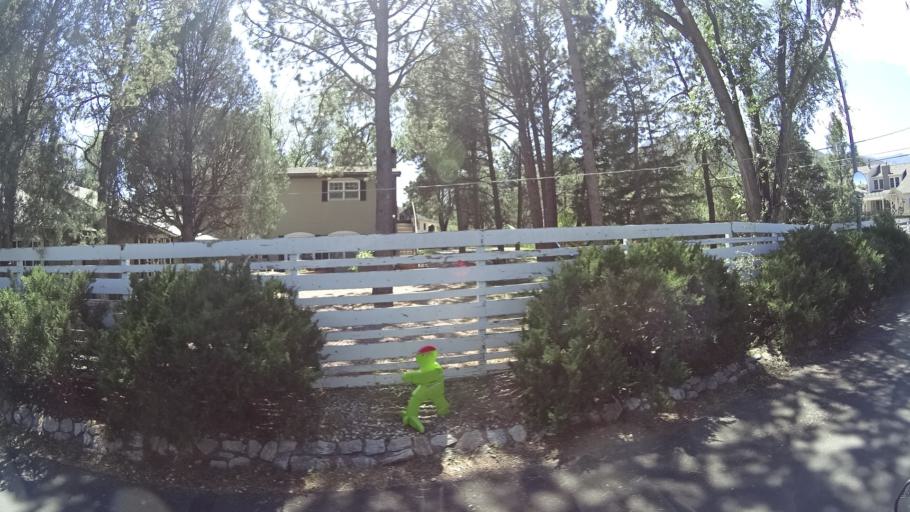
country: US
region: Colorado
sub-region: El Paso County
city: Colorado Springs
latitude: 38.7858
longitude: -104.8360
